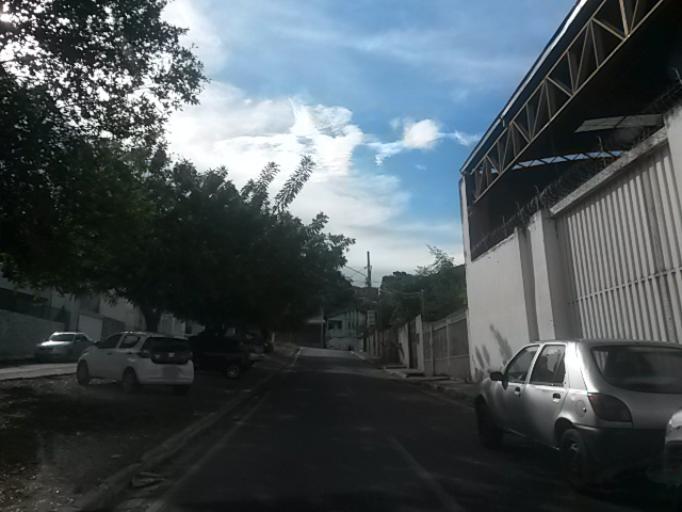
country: BR
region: Mato Grosso
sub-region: Cuiaba
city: Cuiaba
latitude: -15.5975
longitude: -56.0813
